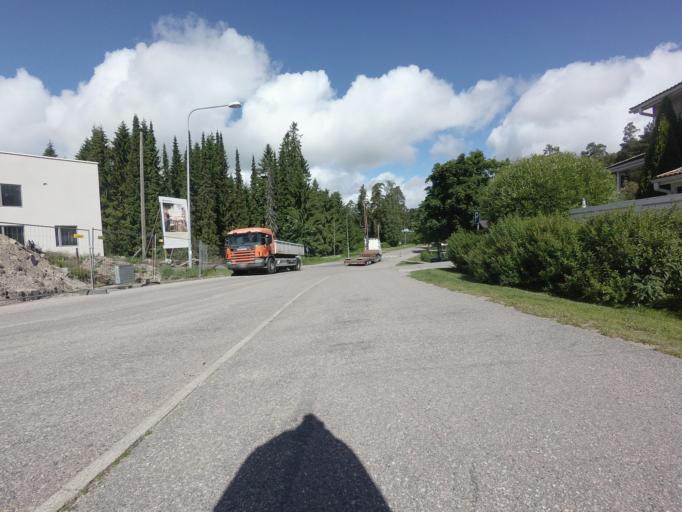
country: FI
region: Uusimaa
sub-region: Helsinki
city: Espoo
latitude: 60.1397
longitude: 24.6430
